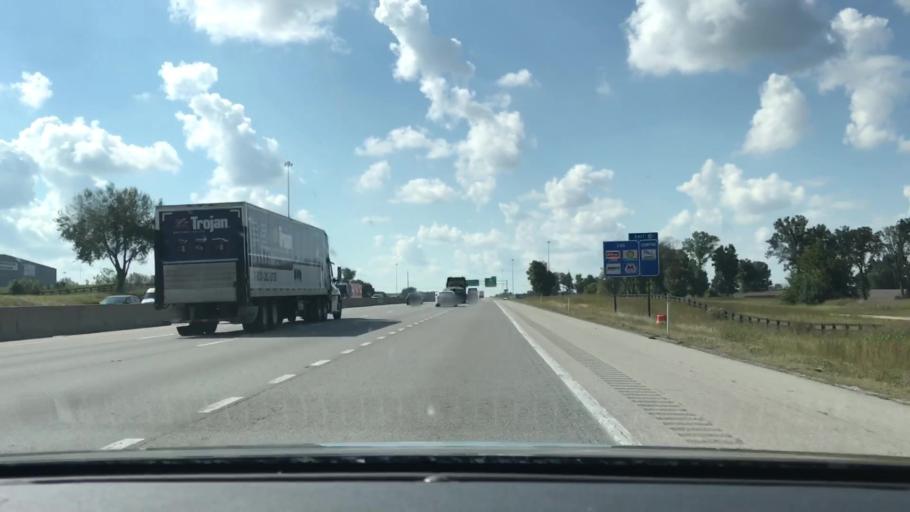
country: US
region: Kentucky
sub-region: Simpson County
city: Franklin
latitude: 36.7217
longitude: -86.5191
